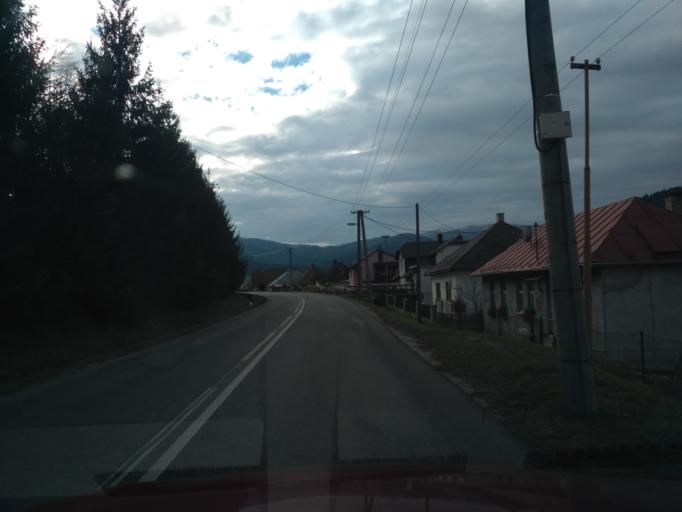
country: SK
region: Kosicky
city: Krompachy
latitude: 48.7998
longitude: 20.7914
